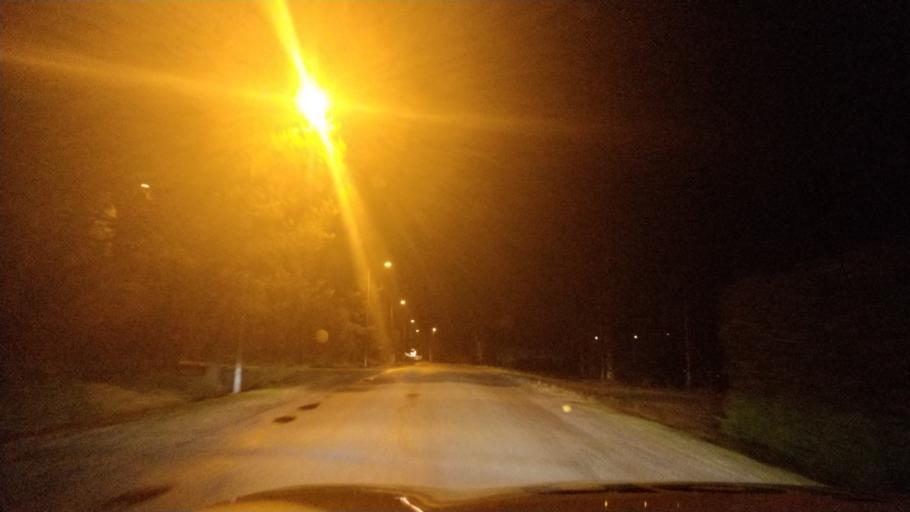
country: FI
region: Uusimaa
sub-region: Helsinki
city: Nurmijaervi
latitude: 60.3802
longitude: 24.6935
